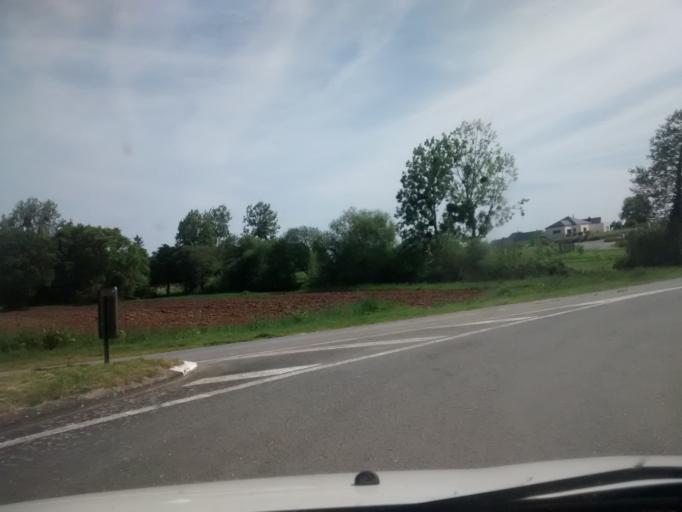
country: FR
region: Brittany
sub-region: Departement d'Ille-et-Vilaine
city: Antrain
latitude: 48.4668
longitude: -1.5098
